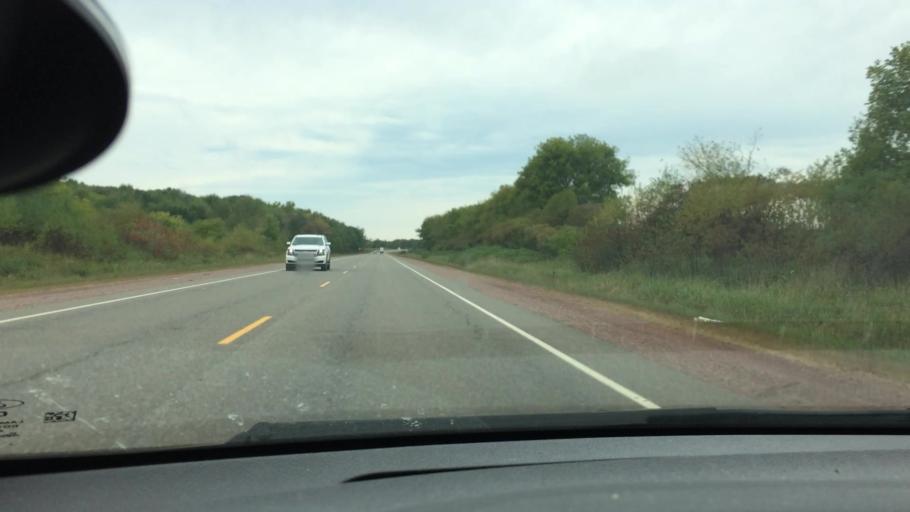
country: US
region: Wisconsin
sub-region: Clark County
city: Neillsville
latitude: 44.5523
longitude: -90.6278
